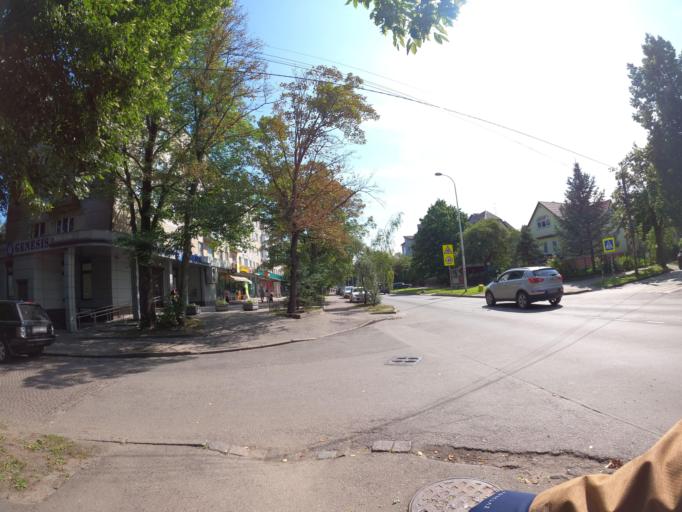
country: RU
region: Kaliningrad
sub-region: Gorod Kaliningrad
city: Kaliningrad
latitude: 54.7360
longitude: 20.5259
